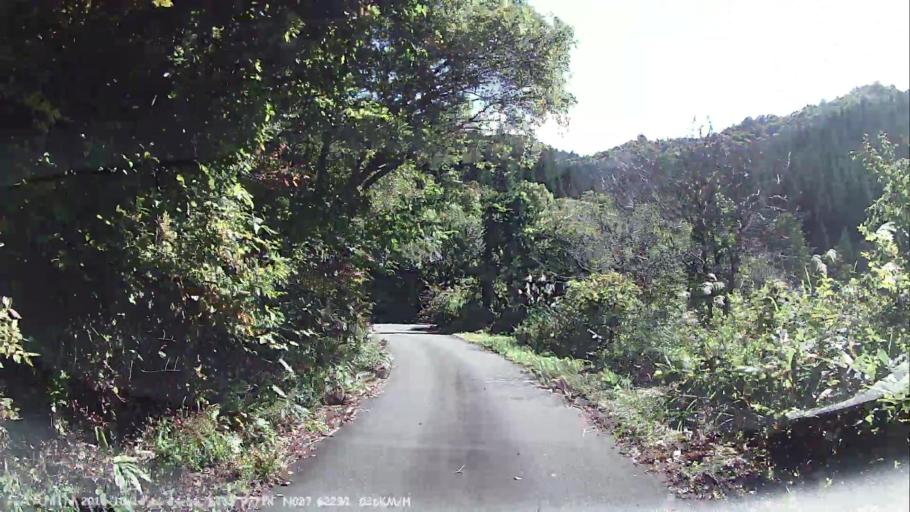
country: JP
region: Fukushima
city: Kitakata
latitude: 37.6229
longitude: 139.9772
